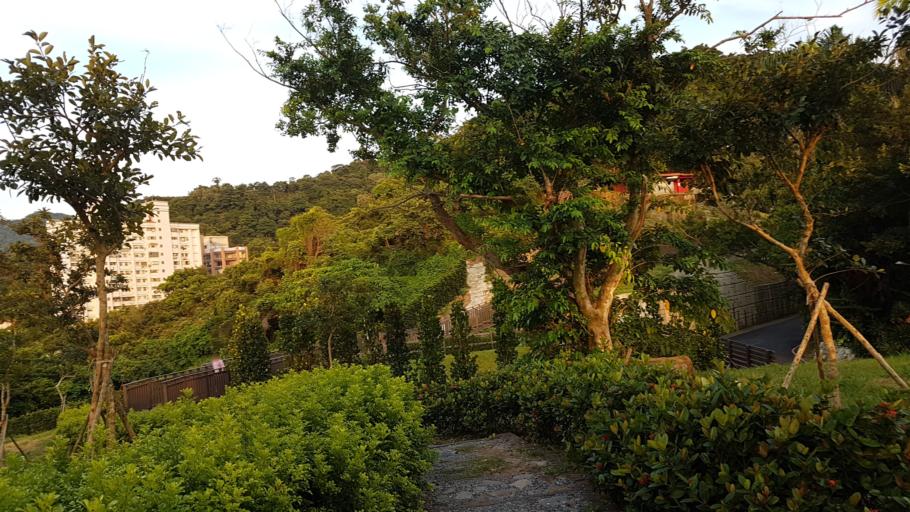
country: TW
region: Taipei
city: Taipei
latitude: 25.0220
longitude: 121.5607
